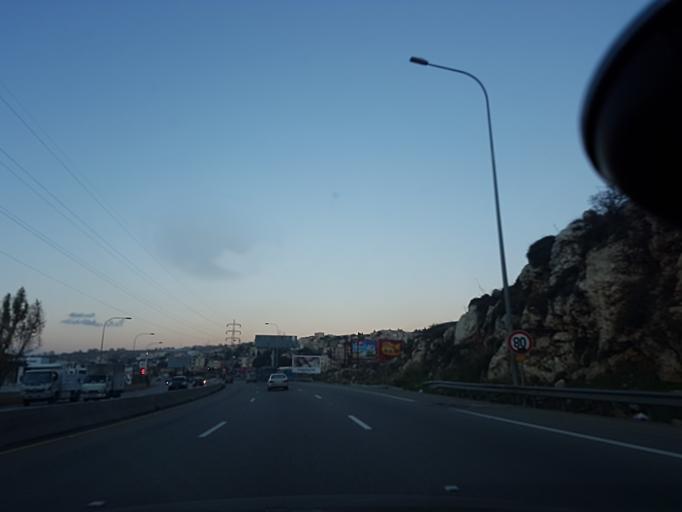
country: LB
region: Liban-Sud
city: Sidon
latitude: 33.6541
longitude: 35.4222
